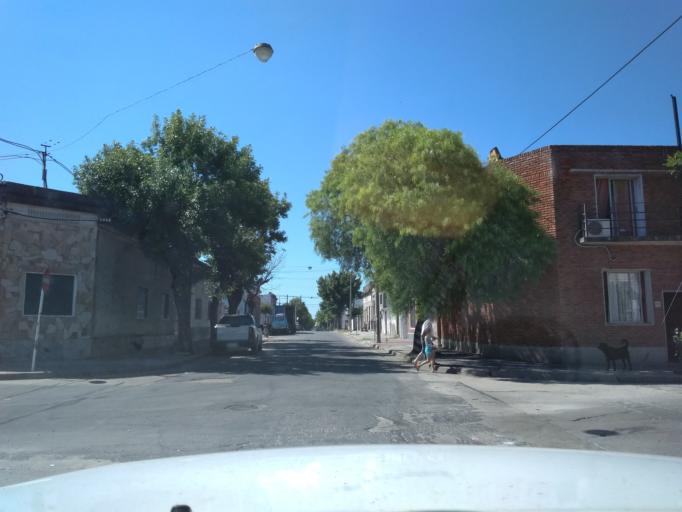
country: UY
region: Florida
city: Florida
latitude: -34.1016
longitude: -56.2179
